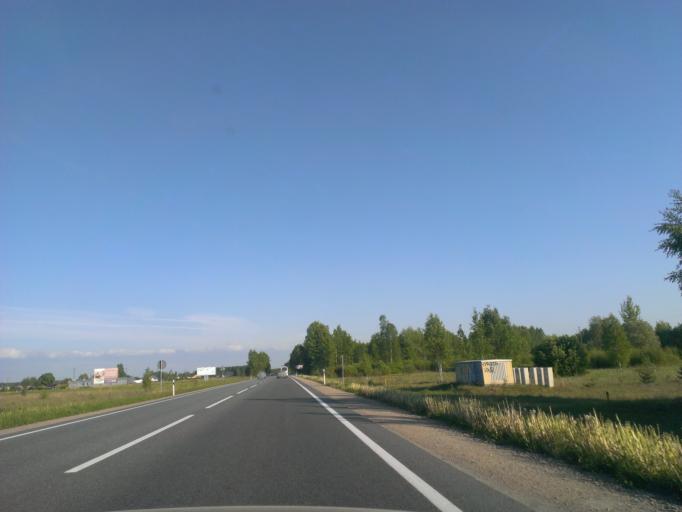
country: LV
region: Kekava
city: Balozi
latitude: 56.8803
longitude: 24.1610
